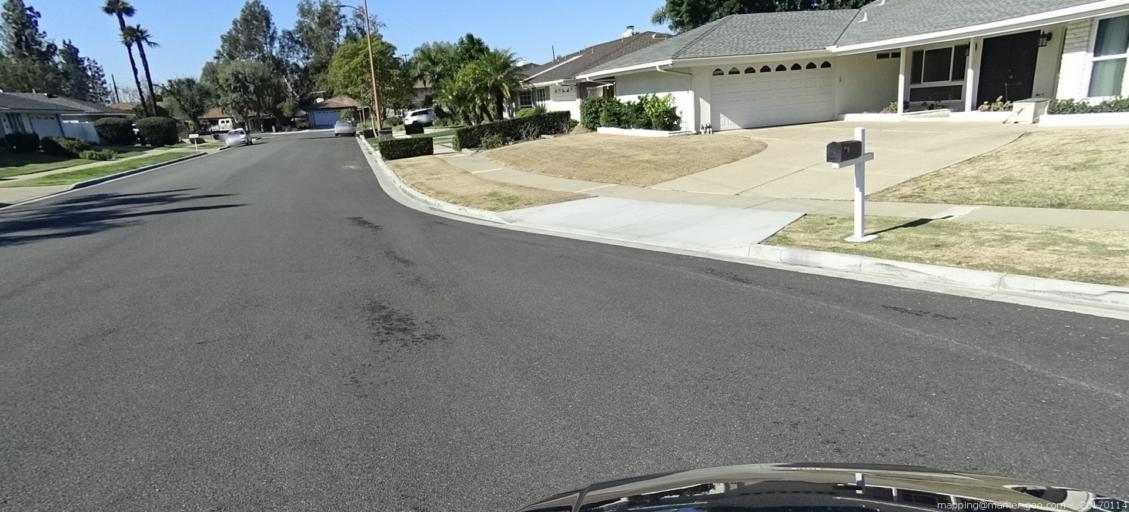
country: US
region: California
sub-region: Orange County
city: North Tustin
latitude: 33.7678
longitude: -117.8020
